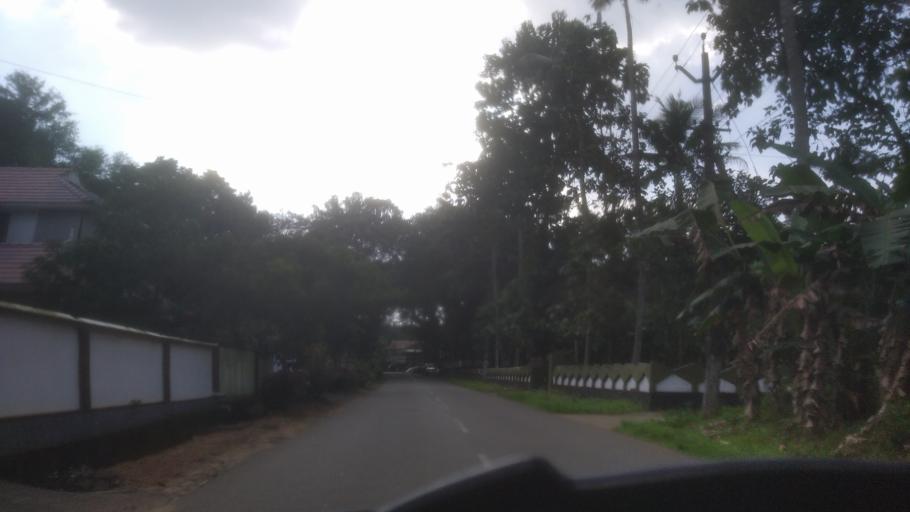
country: IN
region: Kerala
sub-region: Ernakulam
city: Kotamangalam
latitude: 10.0037
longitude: 76.6542
